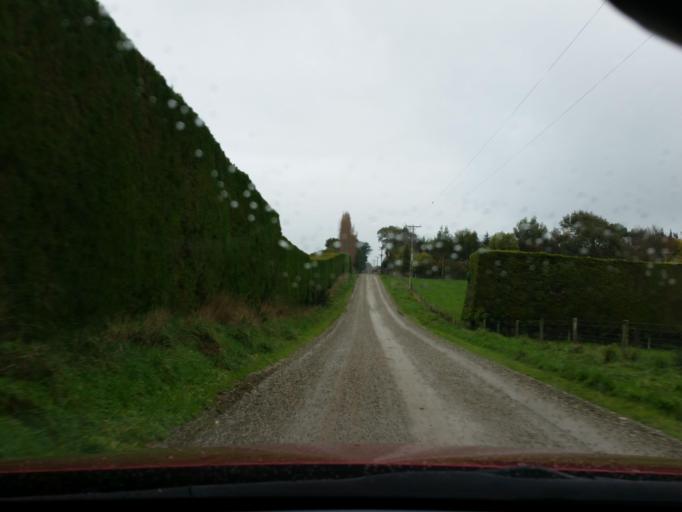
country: NZ
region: Southland
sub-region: Invercargill City
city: Invercargill
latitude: -46.3086
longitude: 168.4789
